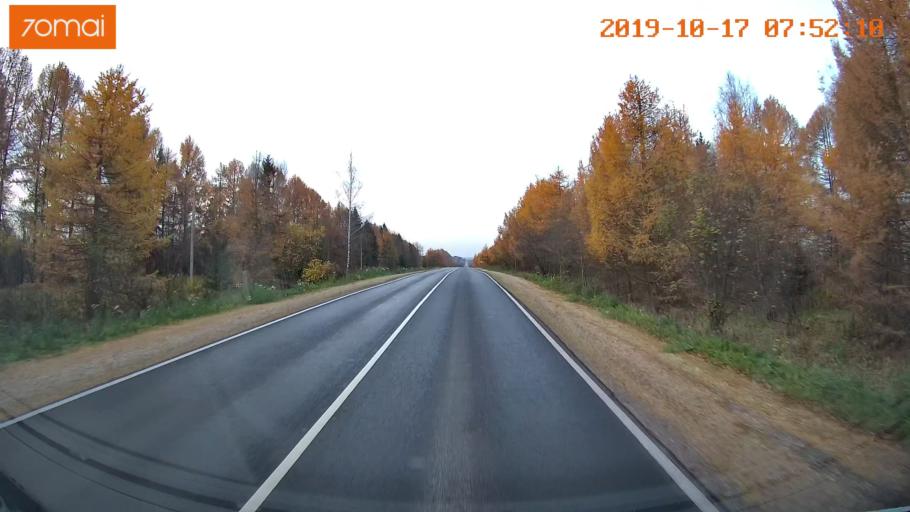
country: RU
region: Vladimir
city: Yur'yev-Pol'skiy
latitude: 56.4753
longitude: 39.6451
